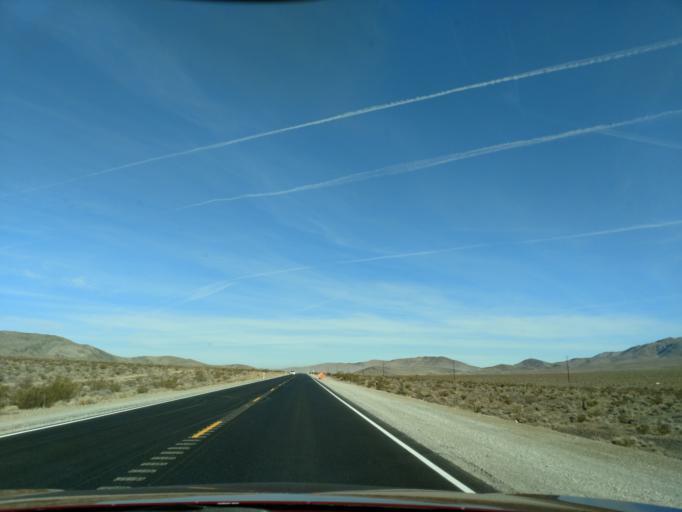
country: US
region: Nevada
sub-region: Nye County
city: Pahrump
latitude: 36.4039
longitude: -116.0680
